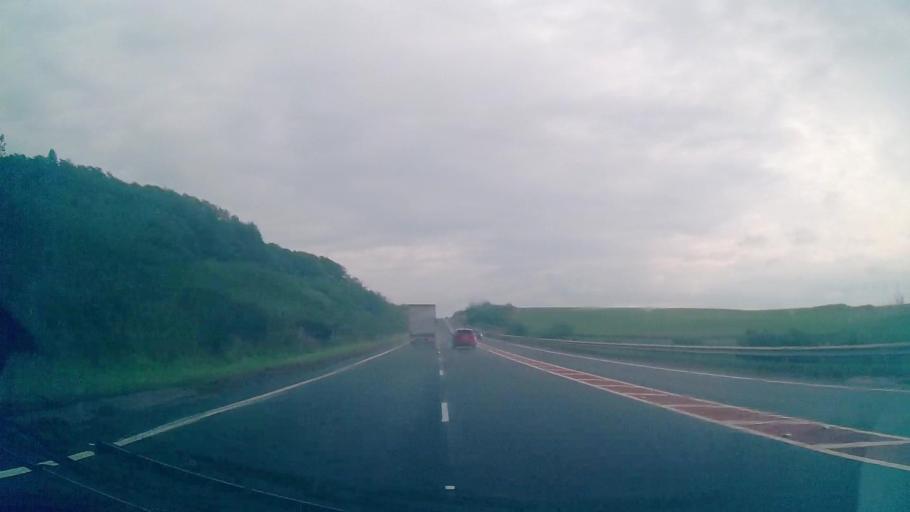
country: GB
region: Scotland
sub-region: Dumfries and Galloway
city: Lockerbie
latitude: 55.0263
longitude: -3.3843
